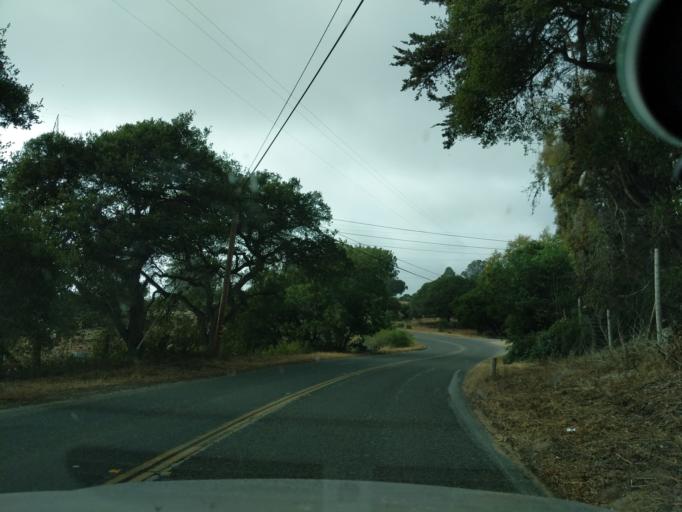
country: US
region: California
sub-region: Monterey County
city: Elkhorn
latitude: 36.8110
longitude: -121.7225
